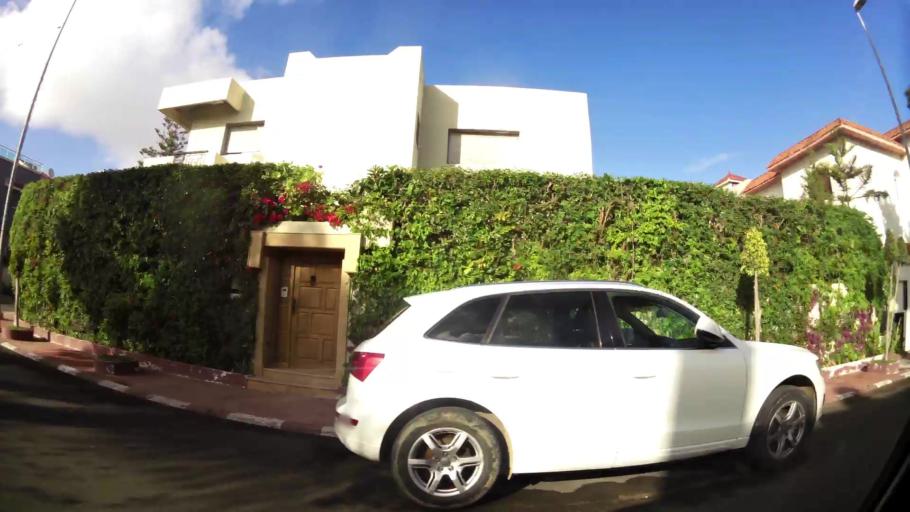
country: MA
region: Grand Casablanca
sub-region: Casablanca
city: Casablanca
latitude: 33.5740
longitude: -7.6868
